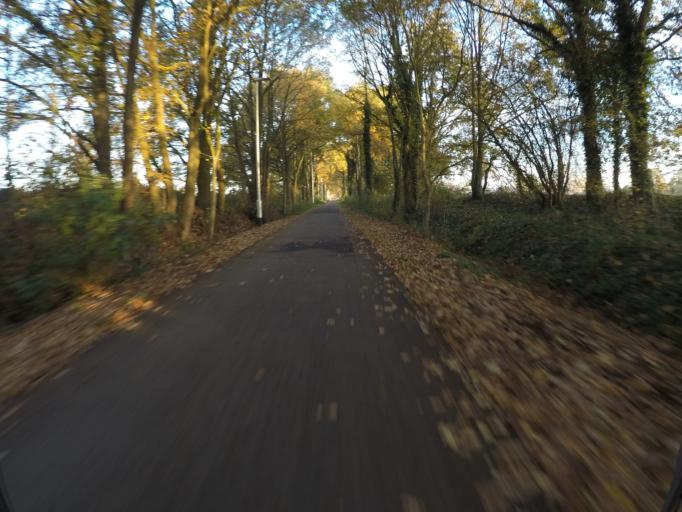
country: BE
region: Flanders
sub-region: Provincie Antwerpen
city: Hulshout
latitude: 51.0948
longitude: 4.8253
